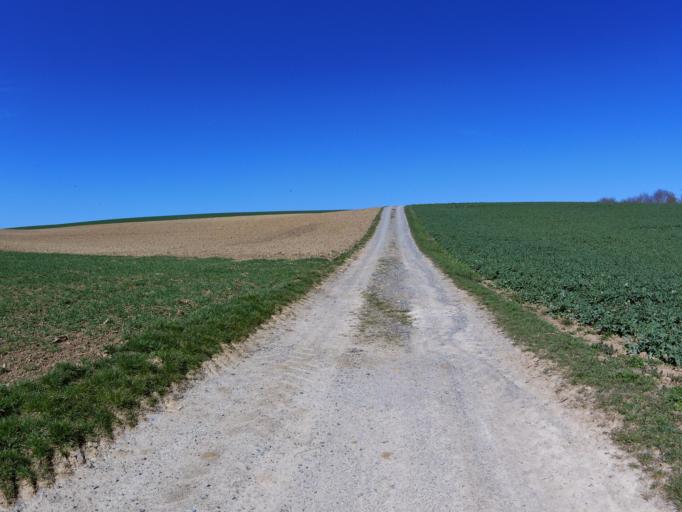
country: DE
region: Bavaria
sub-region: Regierungsbezirk Unterfranken
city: Prosselsheim
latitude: 49.8503
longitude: 10.1379
